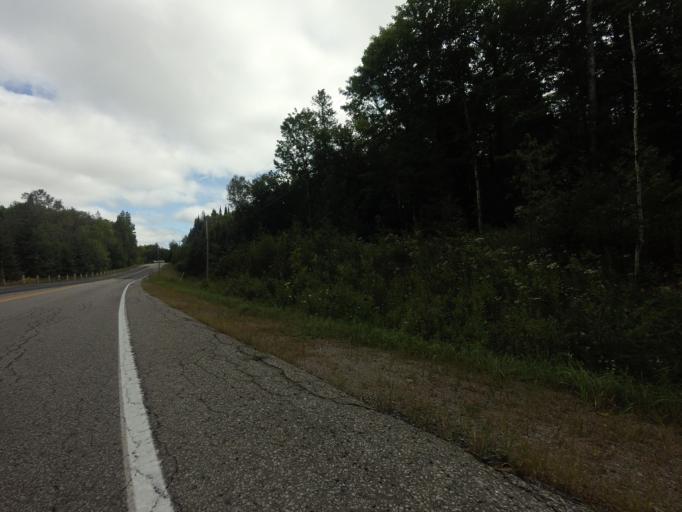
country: CA
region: Ontario
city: Omemee
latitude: 44.8155
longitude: -78.5768
